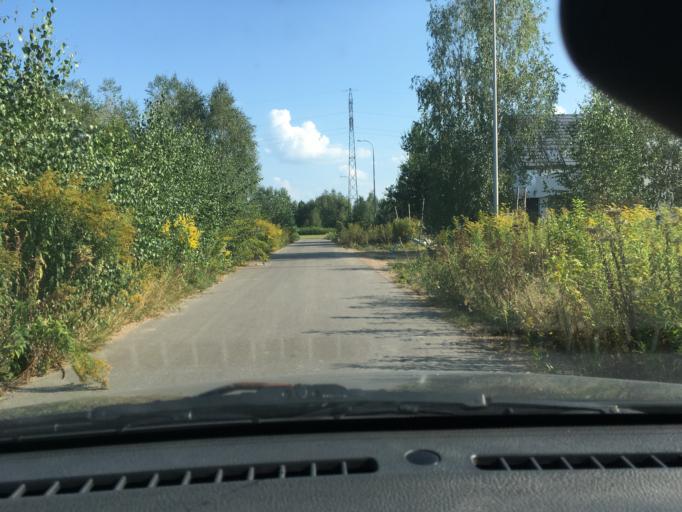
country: PL
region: Masovian Voivodeship
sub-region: Powiat piaseczynski
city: Lesznowola
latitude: 52.0517
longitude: 20.9387
